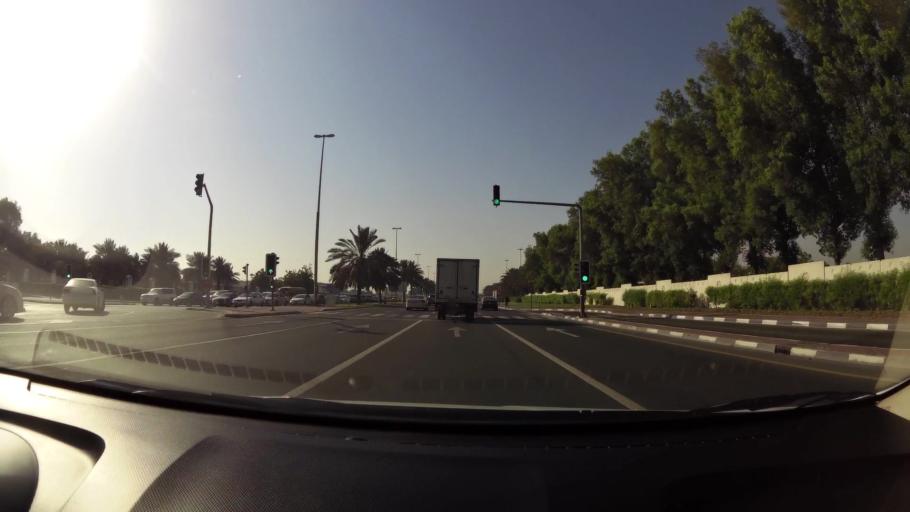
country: AE
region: Ash Shariqah
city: Sharjah
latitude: 25.2719
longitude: 55.3517
